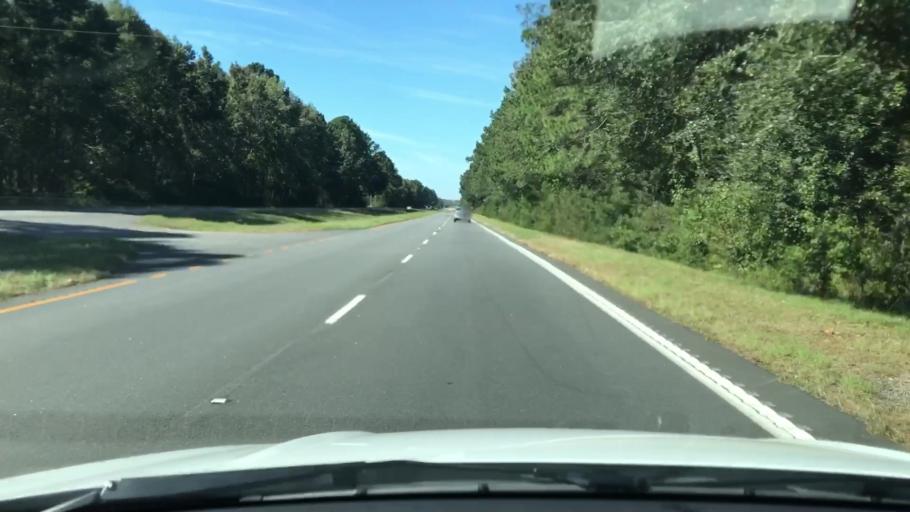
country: US
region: South Carolina
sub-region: Beaufort County
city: Laurel Bay
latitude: 32.5872
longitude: -80.7446
